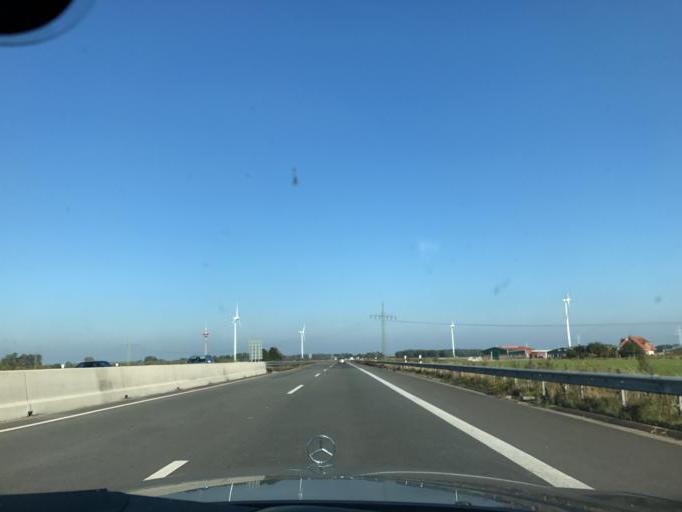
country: DE
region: Lower Saxony
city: Leer
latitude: 53.2461
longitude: 7.4245
